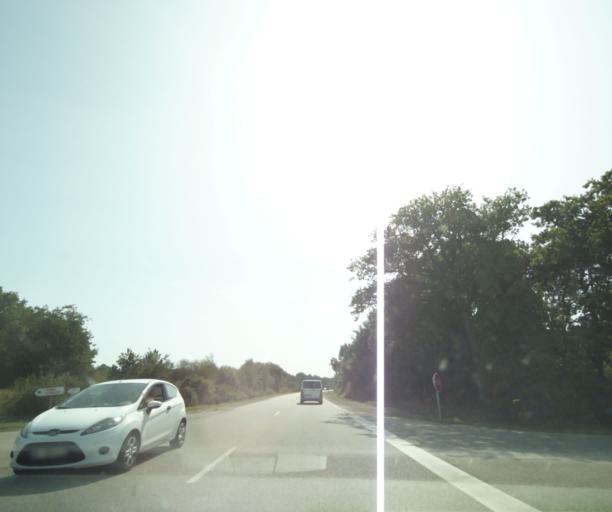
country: FR
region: Brittany
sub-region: Departement du Morbihan
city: Riantec
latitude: 47.7400
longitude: -3.3027
